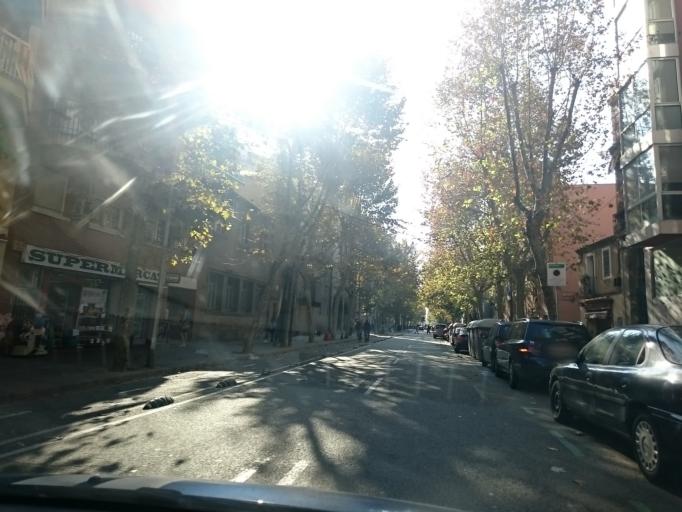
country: ES
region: Catalonia
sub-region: Provincia de Barcelona
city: Sant Marti
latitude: 41.4029
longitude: 2.2024
